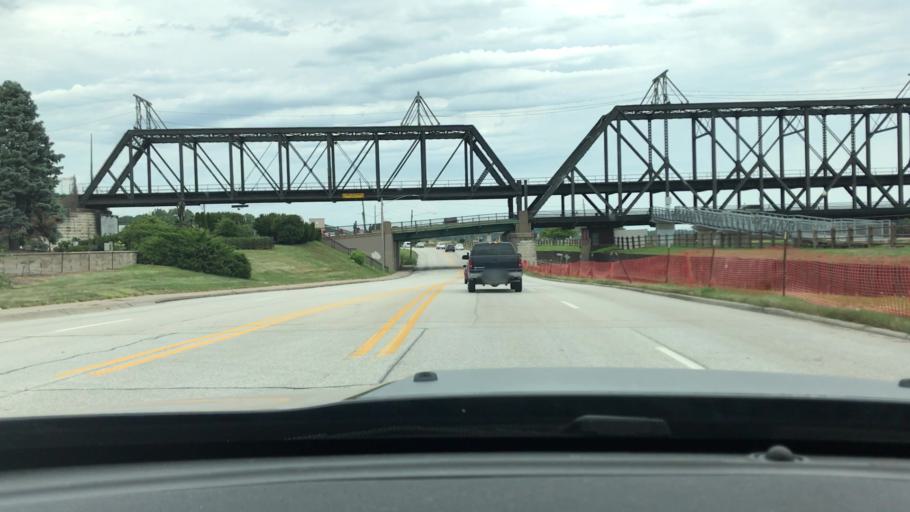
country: US
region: Iowa
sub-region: Scott County
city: Davenport
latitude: 41.5206
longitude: -90.5695
